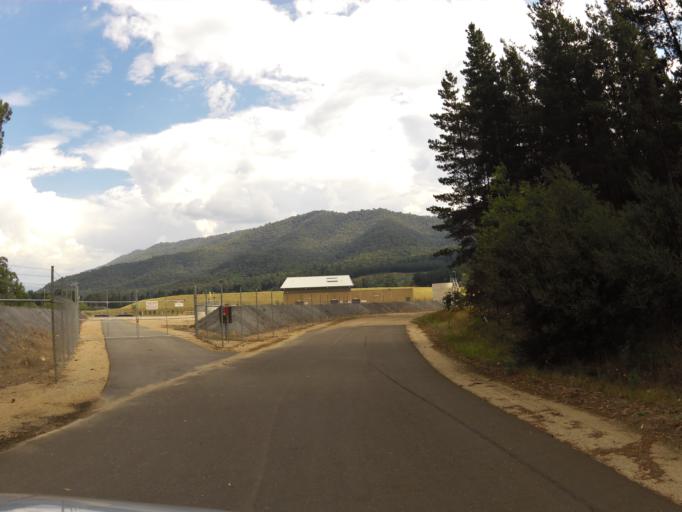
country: AU
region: Victoria
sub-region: Alpine
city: Mount Beauty
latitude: -36.7602
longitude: 147.0230
